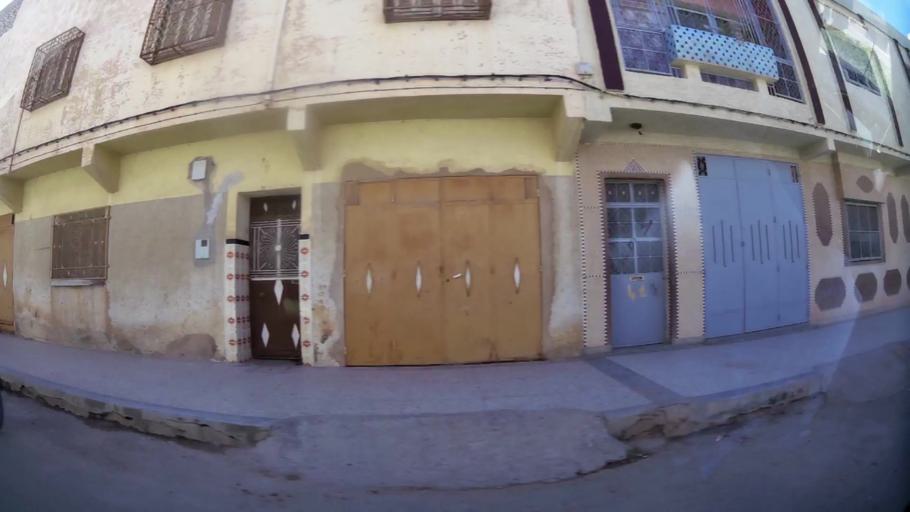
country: MA
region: Oriental
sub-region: Oujda-Angad
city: Oujda
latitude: 34.6833
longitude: -1.9376
